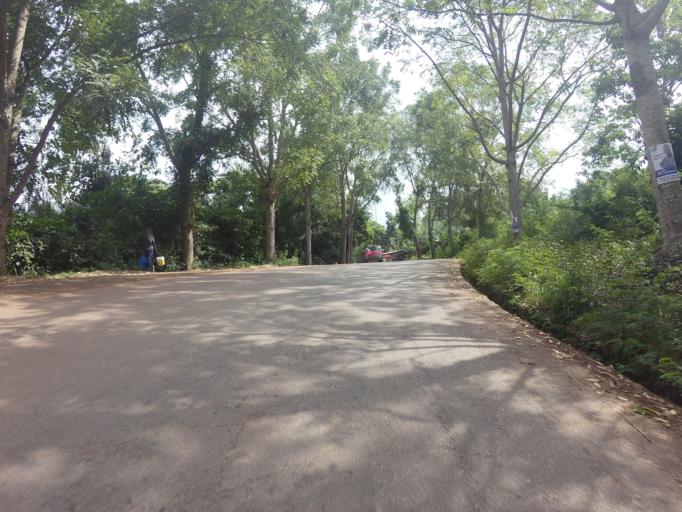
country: GH
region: Eastern
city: Aburi
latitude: 5.9526
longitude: -0.2125
